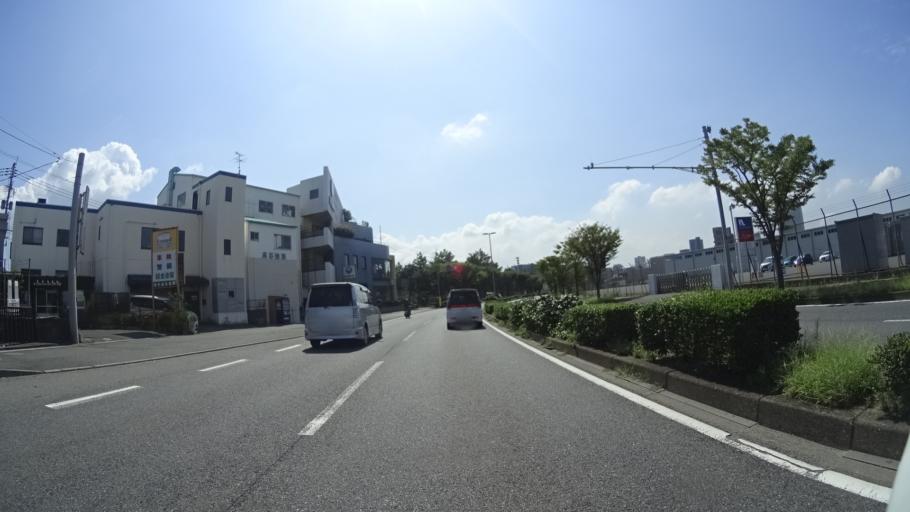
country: JP
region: Fukuoka
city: Kitakyushu
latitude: 33.8879
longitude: 130.8951
